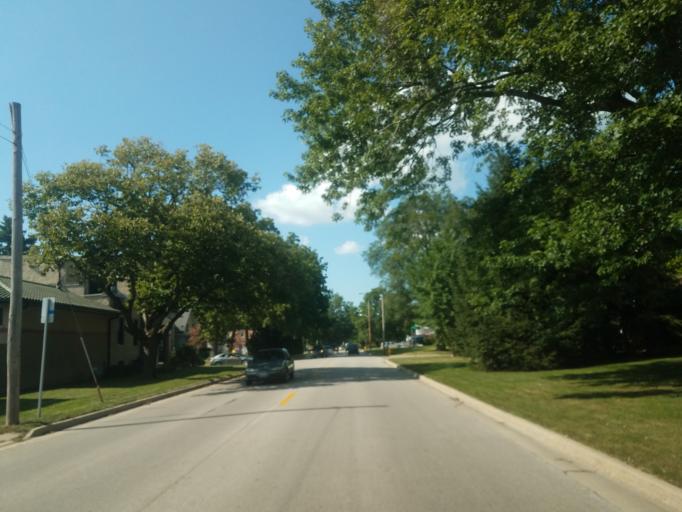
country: US
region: Illinois
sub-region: McLean County
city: Bloomington
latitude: 40.4759
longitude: -88.9628
